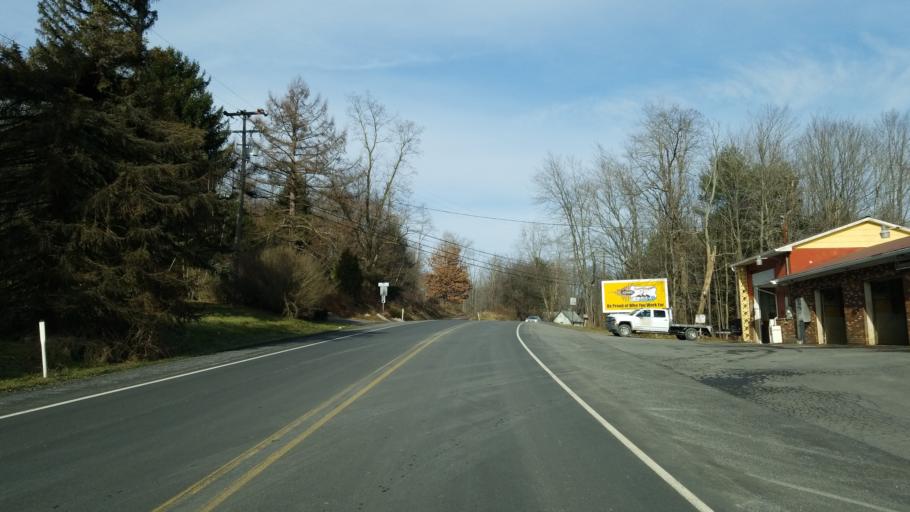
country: US
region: Pennsylvania
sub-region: Clearfield County
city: Curwensville
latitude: 40.9599
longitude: -78.6121
